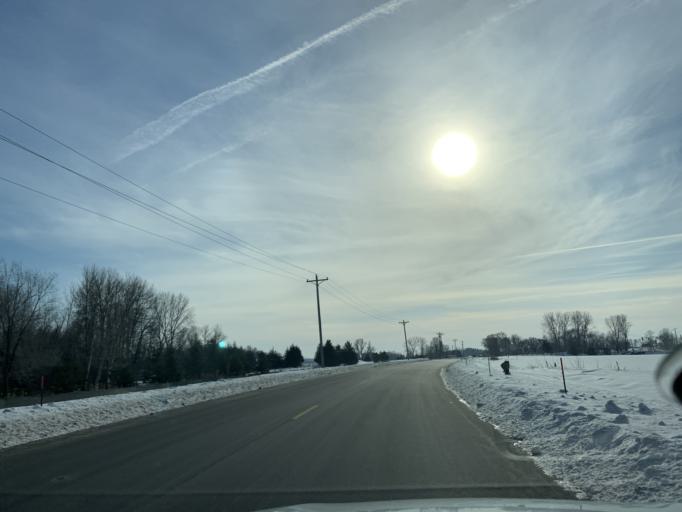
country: US
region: Minnesota
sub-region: Anoka County
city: Columbus
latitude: 45.2539
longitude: -93.0215
